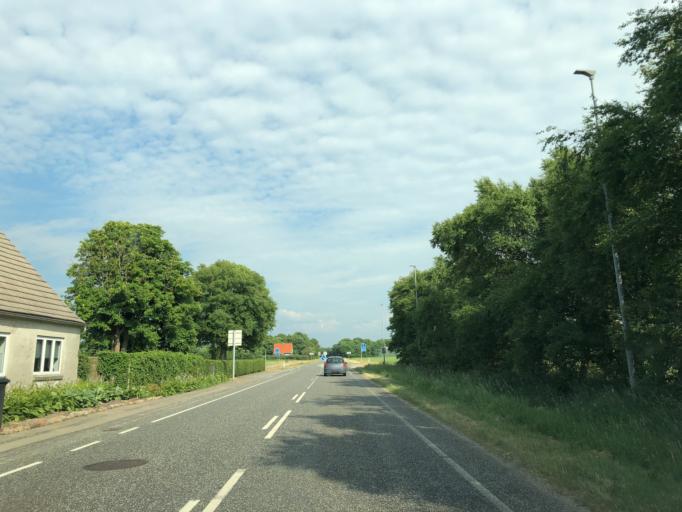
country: DK
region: Central Jutland
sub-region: Ringkobing-Skjern Kommune
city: Skjern
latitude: 55.9019
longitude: 8.4530
